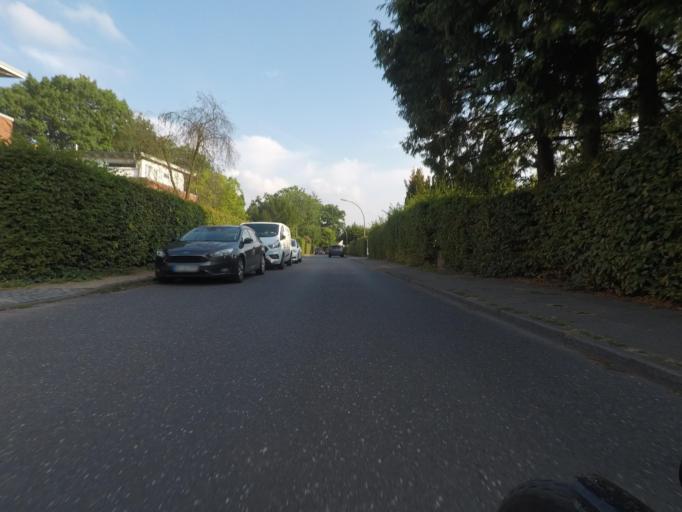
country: DE
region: Hamburg
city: Sasel
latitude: 53.6457
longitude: 10.1102
